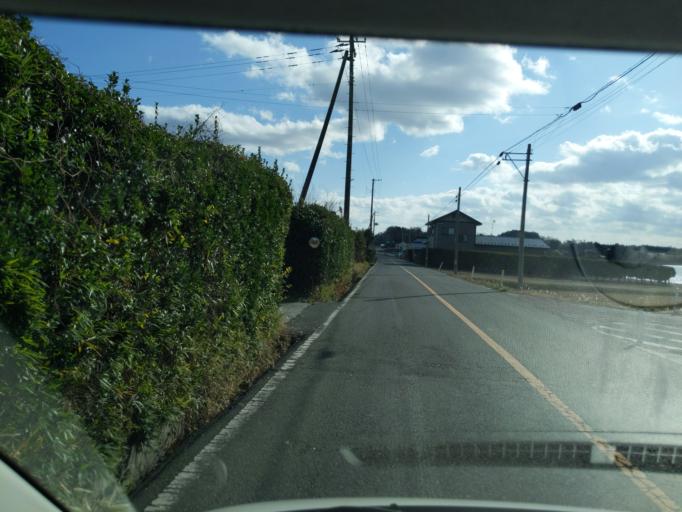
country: JP
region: Miyagi
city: Kogota
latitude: 38.7152
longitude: 141.0812
